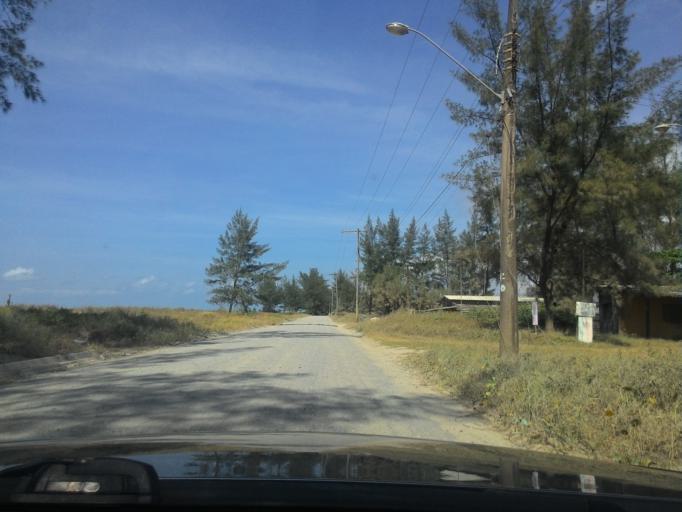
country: BR
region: Sao Paulo
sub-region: Iguape
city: Iguape
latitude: -24.8400
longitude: -47.6808
